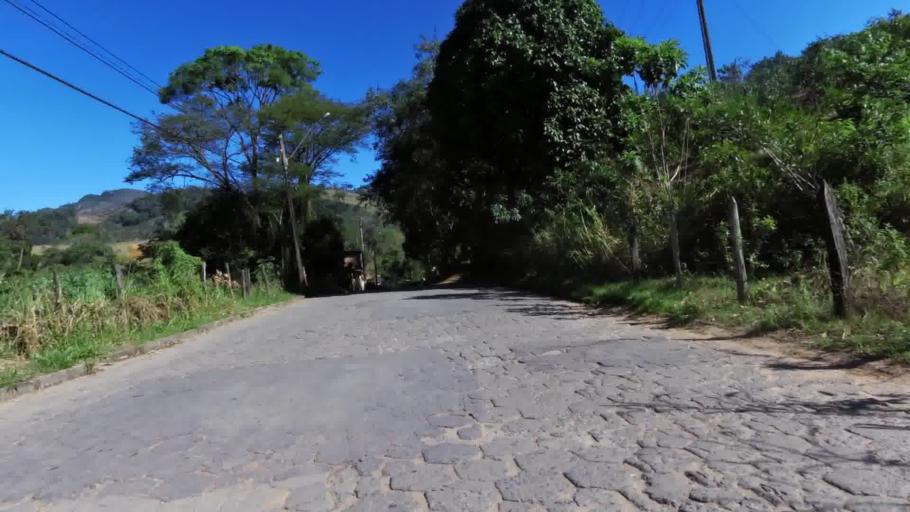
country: BR
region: Espirito Santo
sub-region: Iconha
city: Iconha
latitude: -20.7862
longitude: -40.8226
